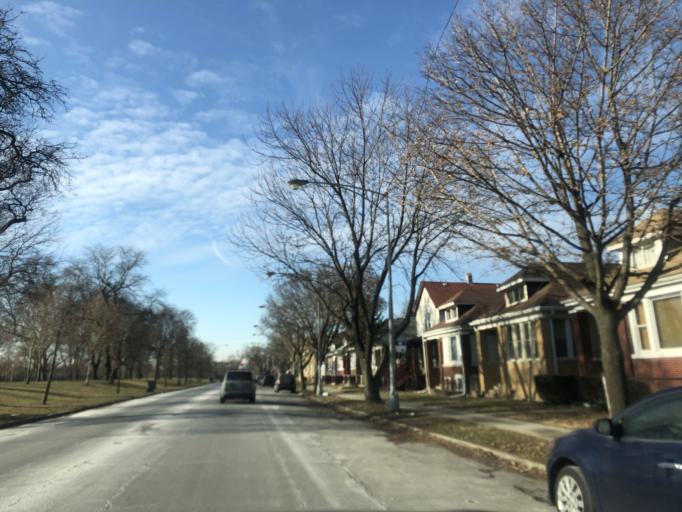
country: US
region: Illinois
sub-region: Cook County
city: Hometown
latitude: 41.7716
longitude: -87.7078
